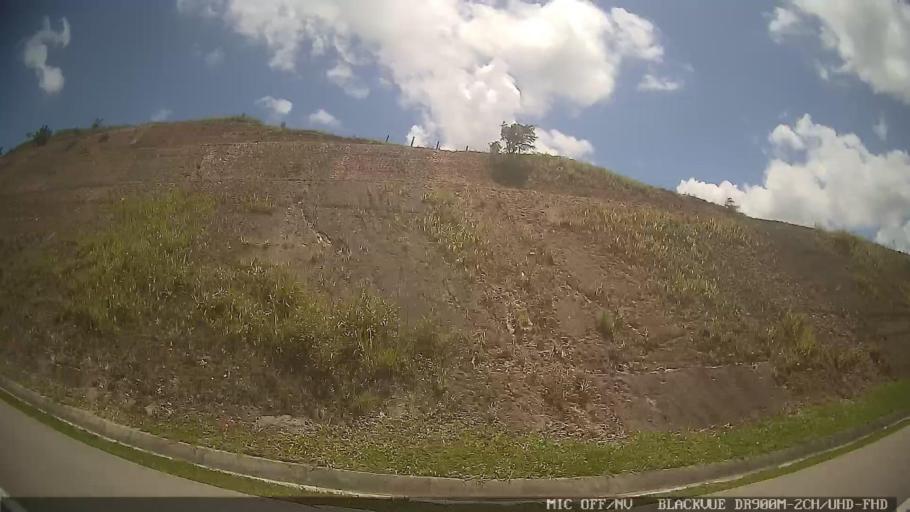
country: BR
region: Sao Paulo
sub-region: Caraguatatuba
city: Caraguatatuba
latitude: -23.4737
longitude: -45.5852
